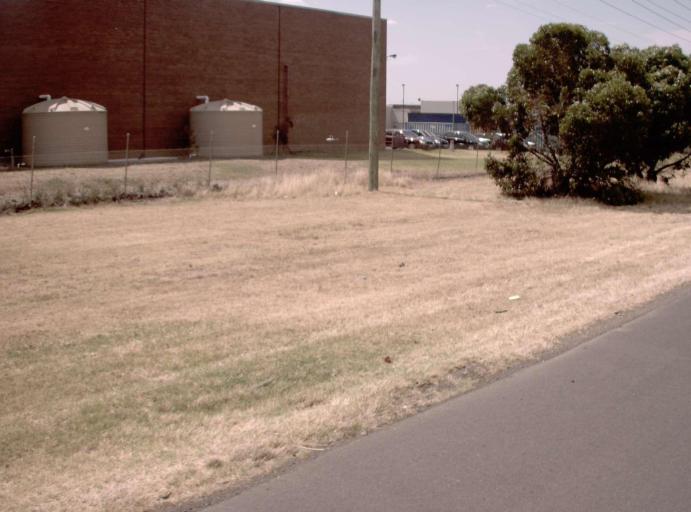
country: AU
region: Victoria
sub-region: Hobsons Bay
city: Laverton
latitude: -37.8361
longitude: 144.8025
